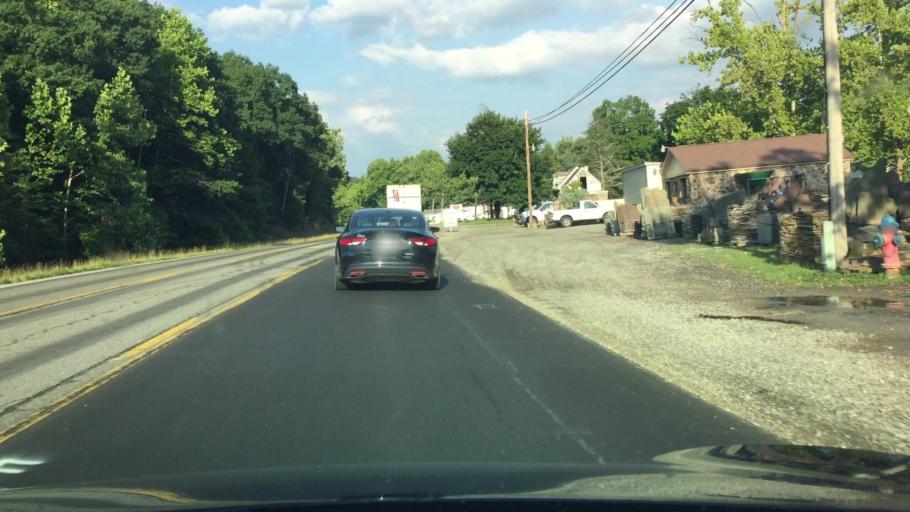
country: US
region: Virginia
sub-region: City of Radford
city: Radford
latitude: 37.1298
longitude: -80.4987
